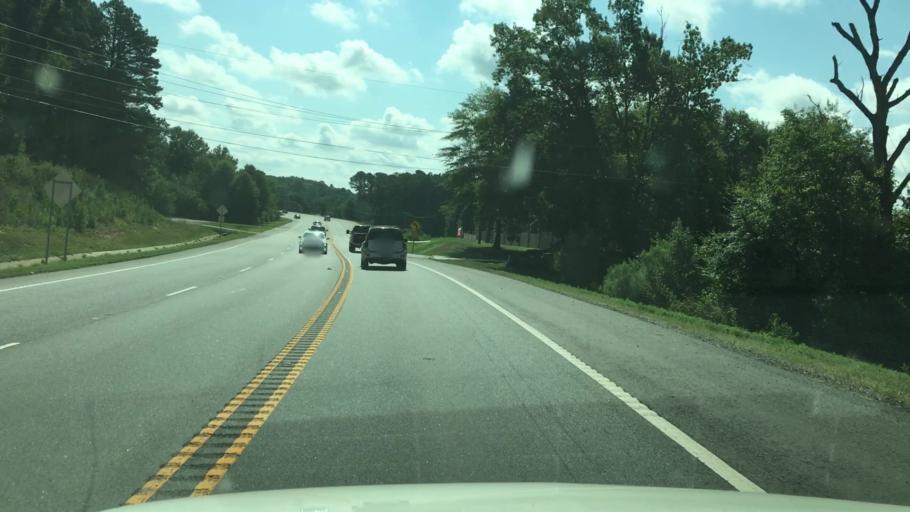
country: US
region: Arkansas
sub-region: Garland County
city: Piney
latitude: 34.5077
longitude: -93.1894
